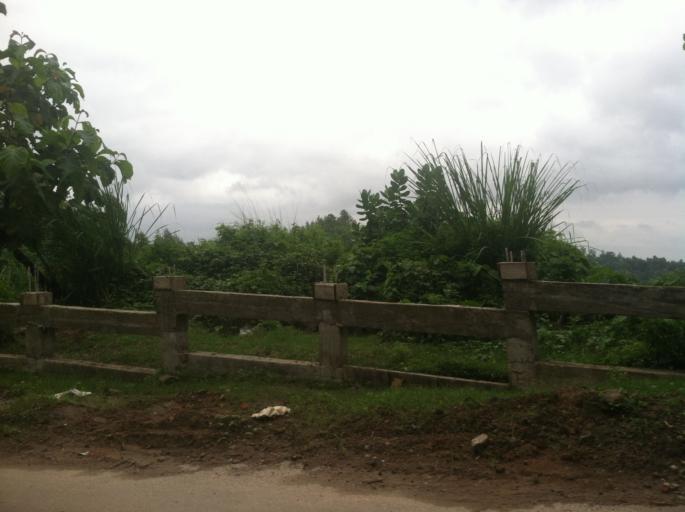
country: BD
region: Chittagong
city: Raojan
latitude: 22.6444
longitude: 92.1290
